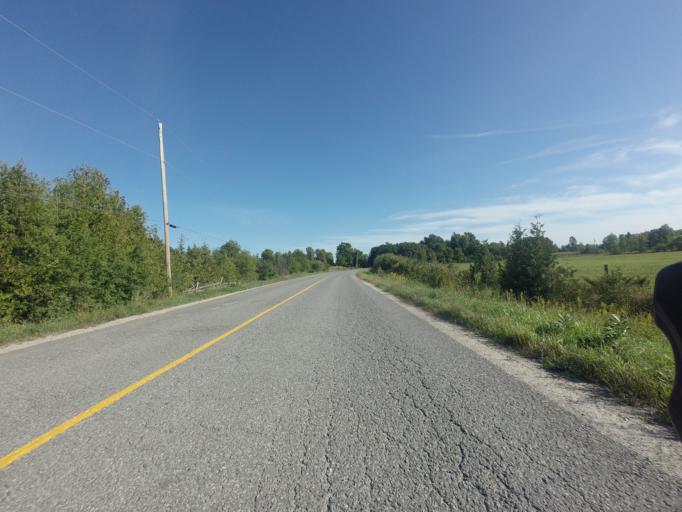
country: CA
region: Ontario
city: Perth
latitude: 44.9207
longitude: -76.3569
